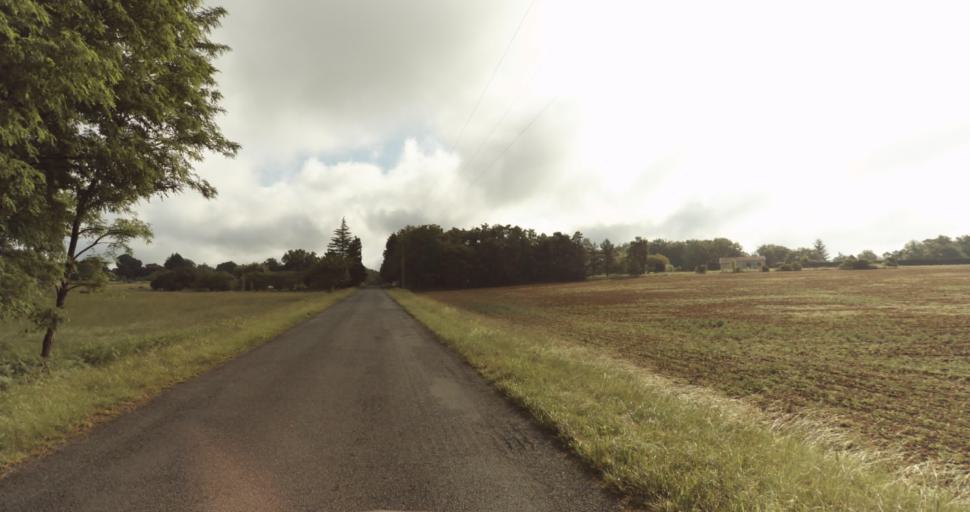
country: FR
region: Aquitaine
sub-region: Departement de la Dordogne
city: Le Bugue
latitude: 44.9208
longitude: 0.8209
